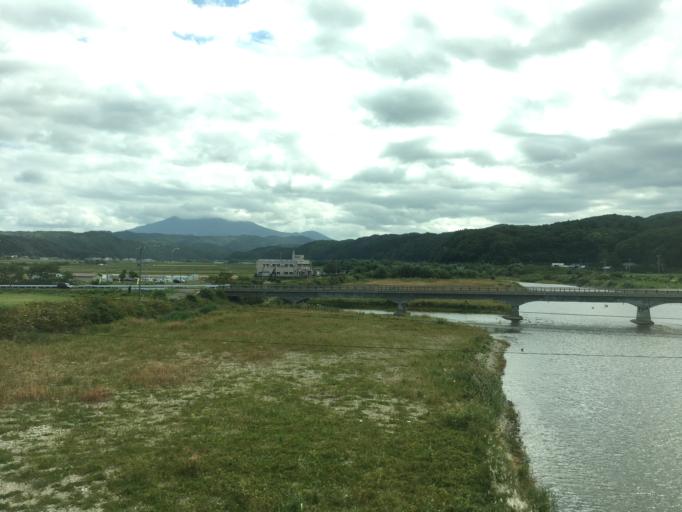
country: JP
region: Aomori
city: Shimokizukuri
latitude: 40.7594
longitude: 140.1584
